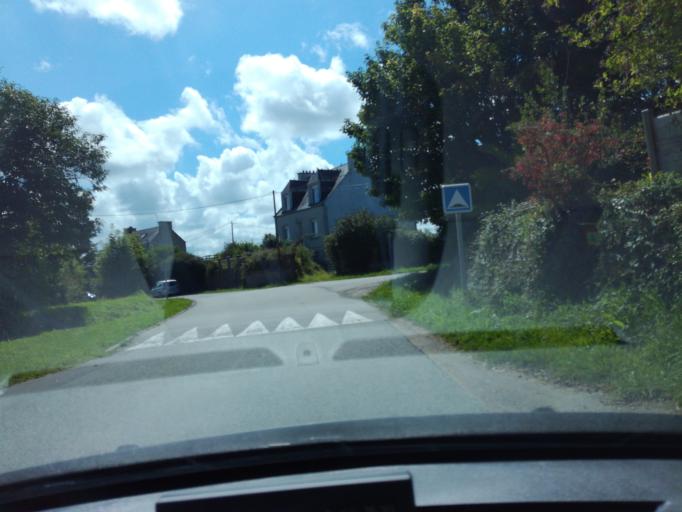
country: FR
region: Brittany
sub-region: Departement du Finistere
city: Saint-Pabu
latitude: 48.5611
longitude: -4.6027
